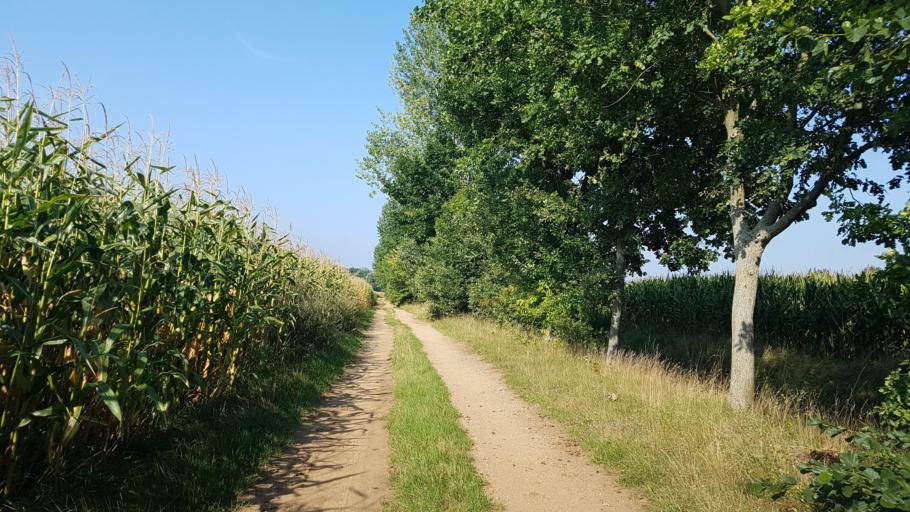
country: DE
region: Brandenburg
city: Luckau
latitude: 51.7981
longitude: 13.6598
